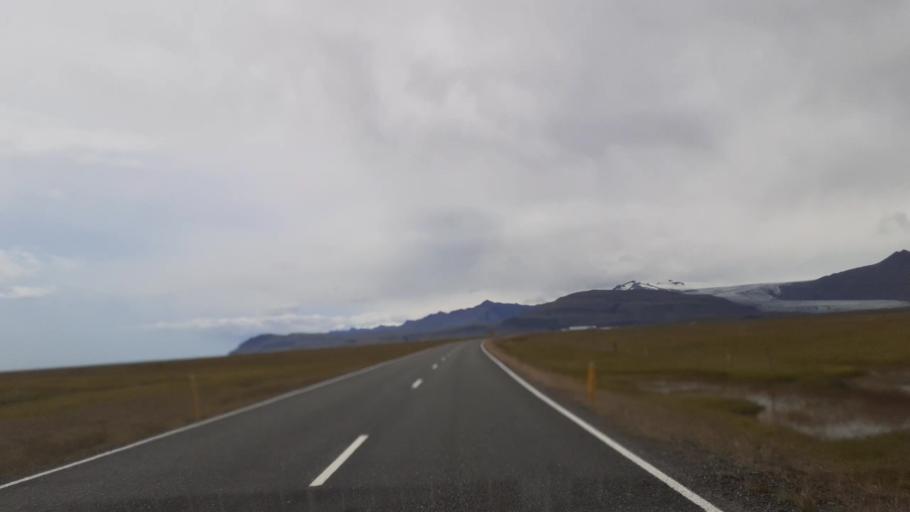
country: IS
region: East
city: Hoefn
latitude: 64.2643
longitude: -15.5174
